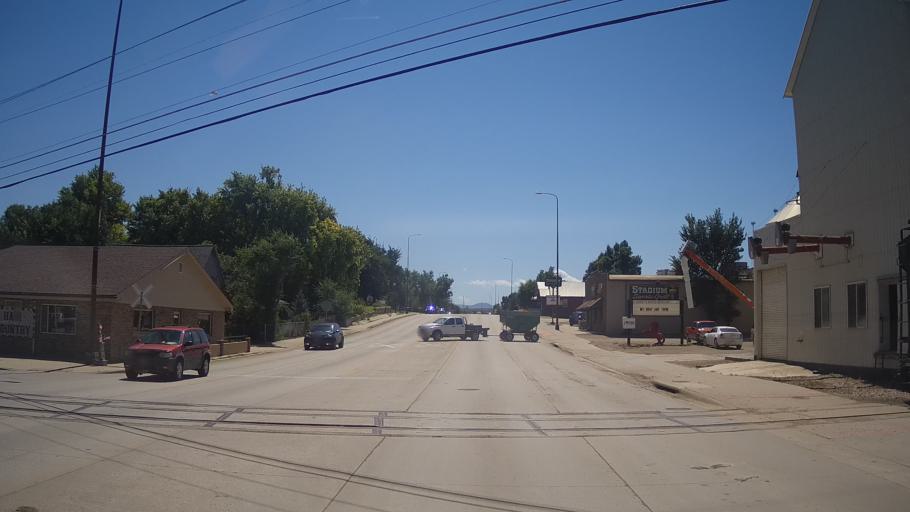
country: US
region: South Dakota
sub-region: Butte County
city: Belle Fourche
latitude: 44.6703
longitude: -103.8536
